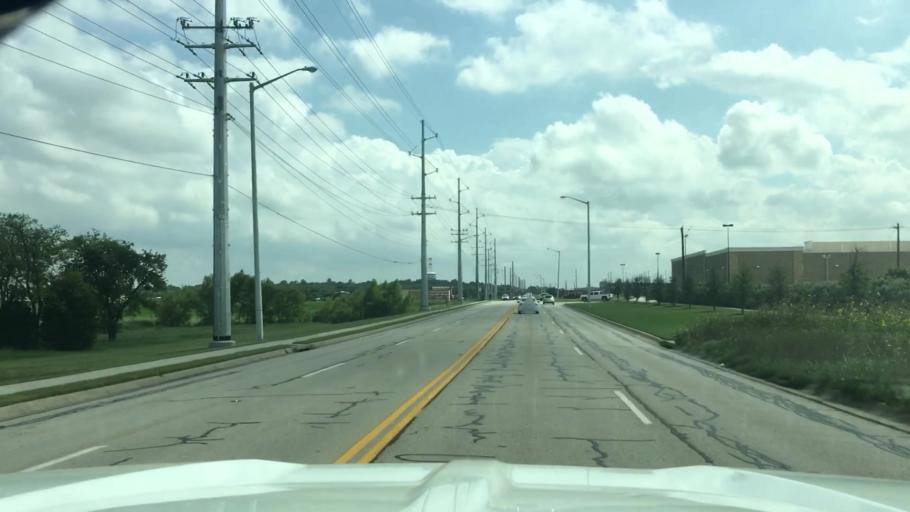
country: US
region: Texas
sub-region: Denton County
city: Denton
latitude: 33.2340
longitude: -97.1609
